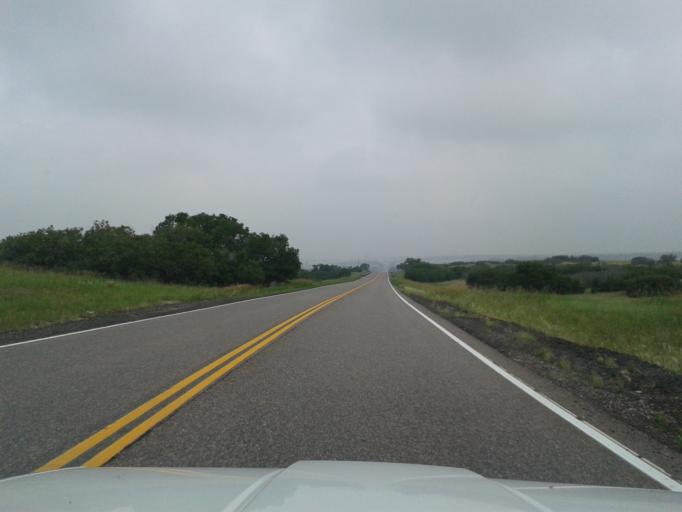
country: US
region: Colorado
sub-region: Douglas County
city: The Pinery
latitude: 39.3622
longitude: -104.7474
